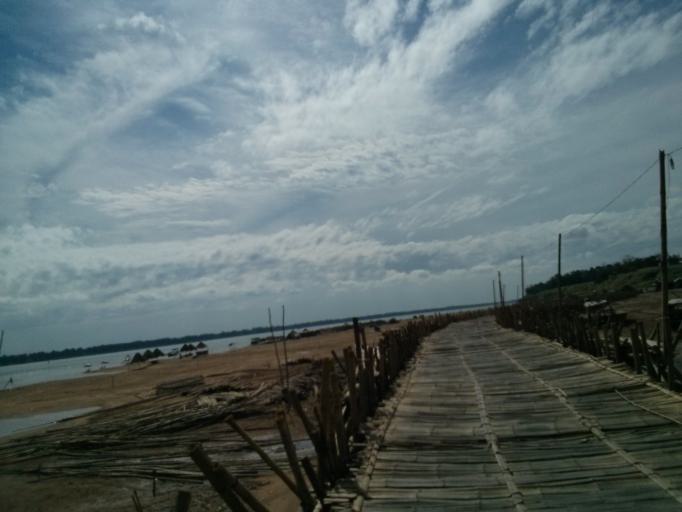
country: KH
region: Kampong Cham
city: Kampong Cham
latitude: 11.9722
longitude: 105.4629
